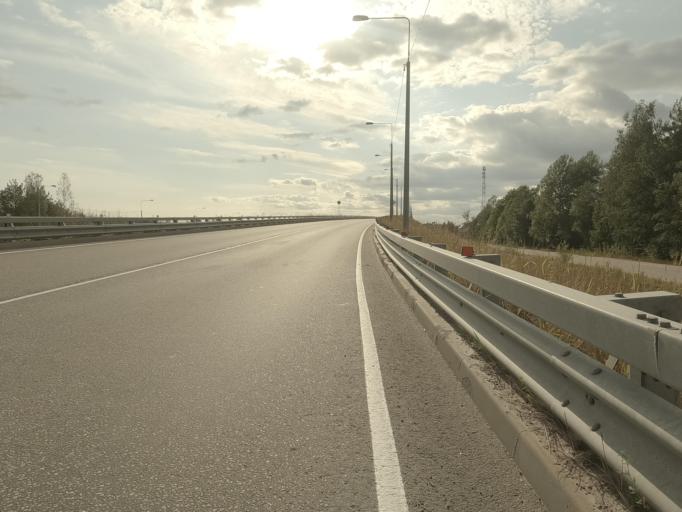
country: RU
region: Leningrad
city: Lesogorskiy
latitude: 60.8567
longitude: 28.9532
